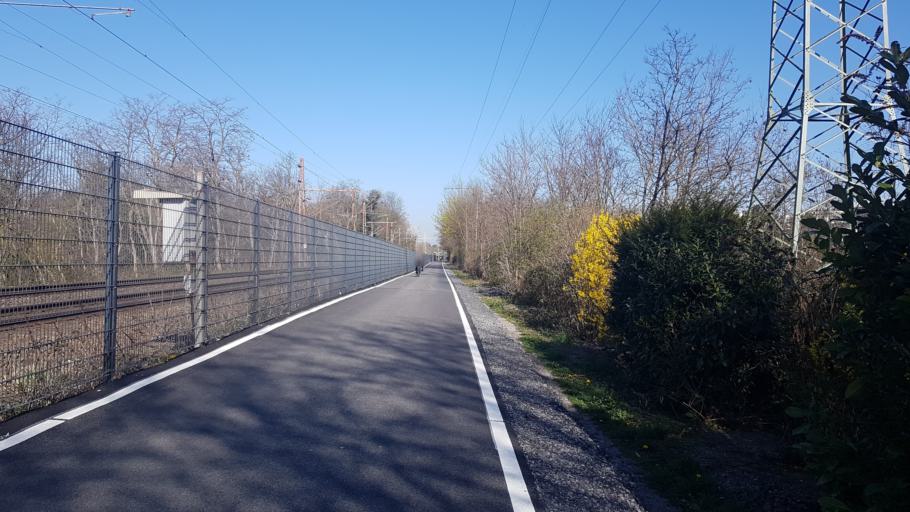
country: DE
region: North Rhine-Westphalia
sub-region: Regierungsbezirk Dusseldorf
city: Essen
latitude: 51.4681
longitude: 6.9531
